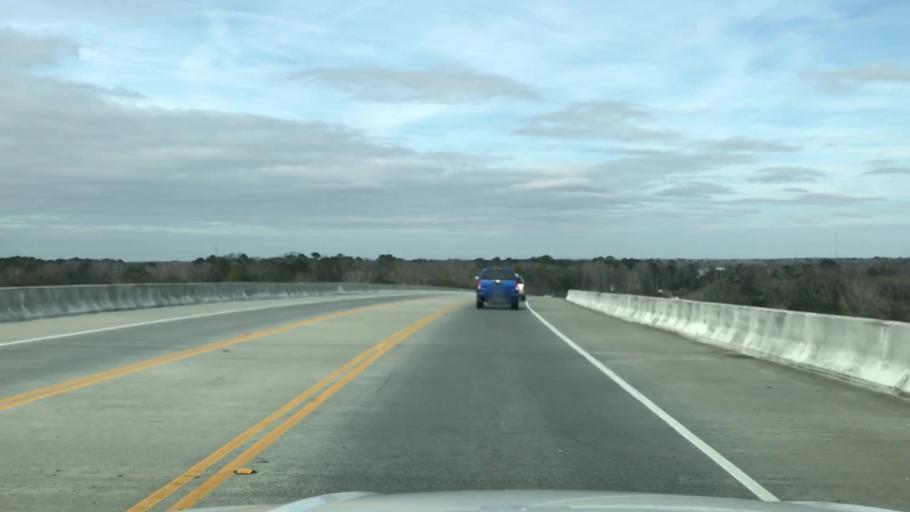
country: US
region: South Carolina
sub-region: Charleston County
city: Shell Point
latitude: 32.7860
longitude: -80.1076
